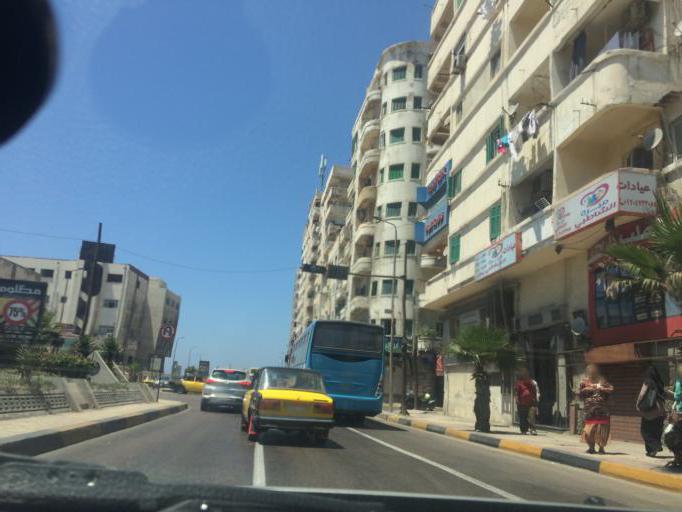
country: EG
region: Alexandria
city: Alexandria
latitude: 31.2084
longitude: 29.9131
